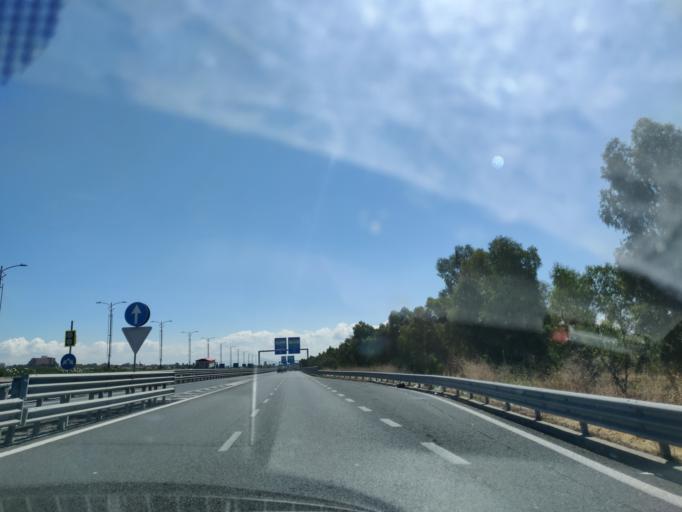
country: IT
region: Latium
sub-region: Citta metropolitana di Roma Capitale
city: Vitinia
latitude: 41.8165
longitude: 12.3733
